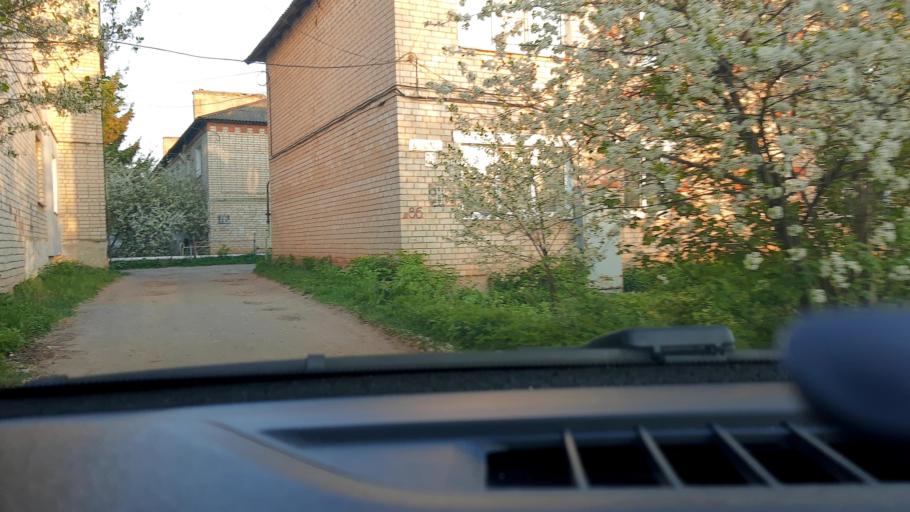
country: RU
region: Nizjnij Novgorod
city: Neklyudovo
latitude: 56.4151
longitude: 43.9792
